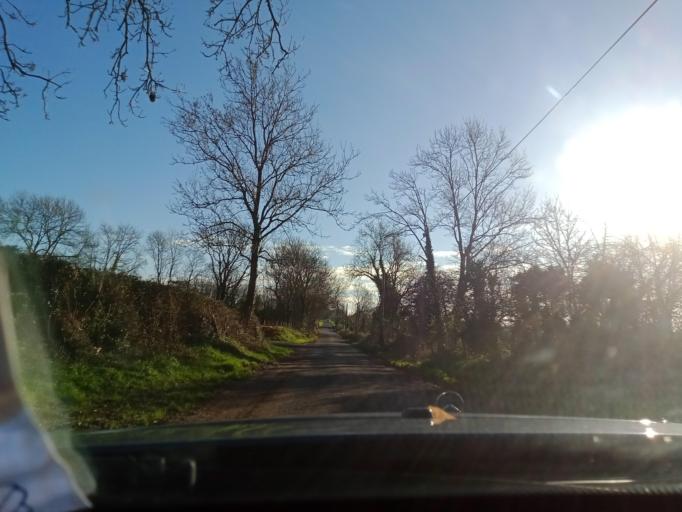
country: IE
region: Leinster
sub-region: Kilkenny
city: Mooncoin
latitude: 52.3403
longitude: -7.2691
